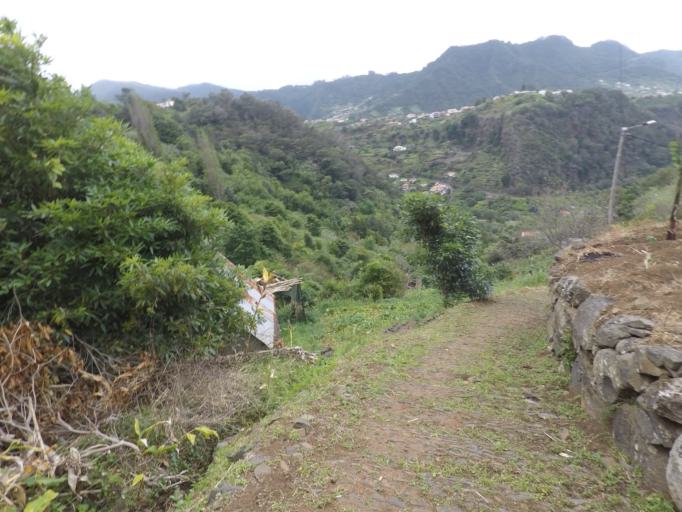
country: PT
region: Madeira
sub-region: Santana
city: Santana
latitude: 32.7717
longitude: -16.8456
